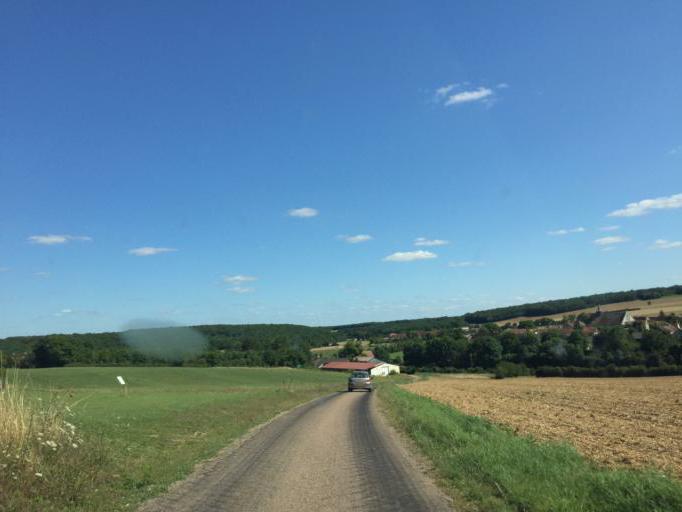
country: FR
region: Bourgogne
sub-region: Departement de l'Yonne
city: Fontenailles
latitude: 47.5630
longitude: 3.3270
